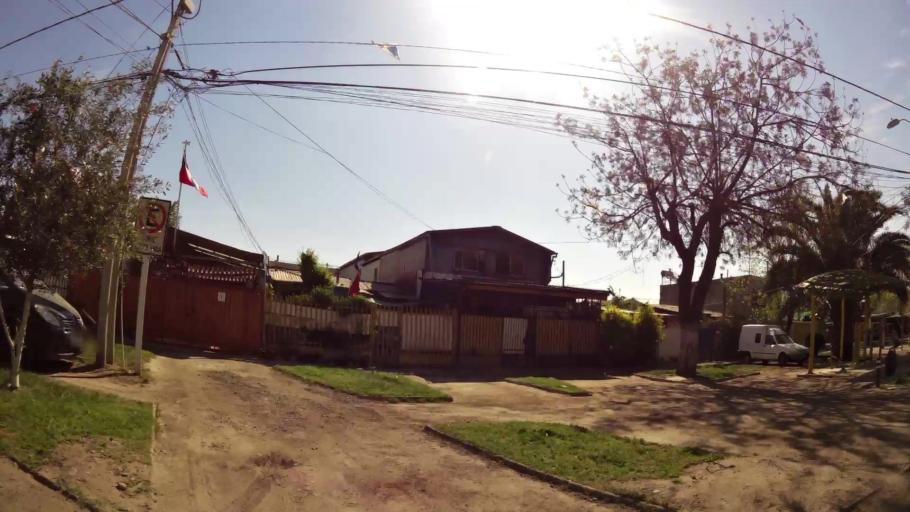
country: CL
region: Santiago Metropolitan
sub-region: Provincia de Santiago
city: La Pintana
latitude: -33.5335
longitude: -70.6092
